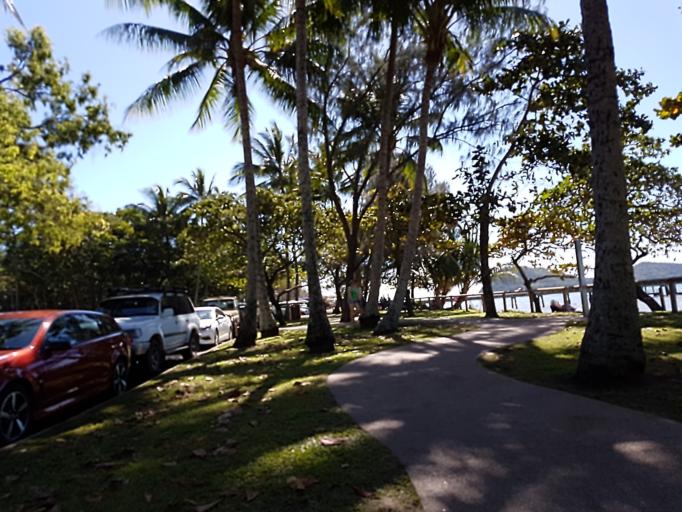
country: AU
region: Queensland
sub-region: Cairns
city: Palm Cove
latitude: -16.7410
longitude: 145.6714
